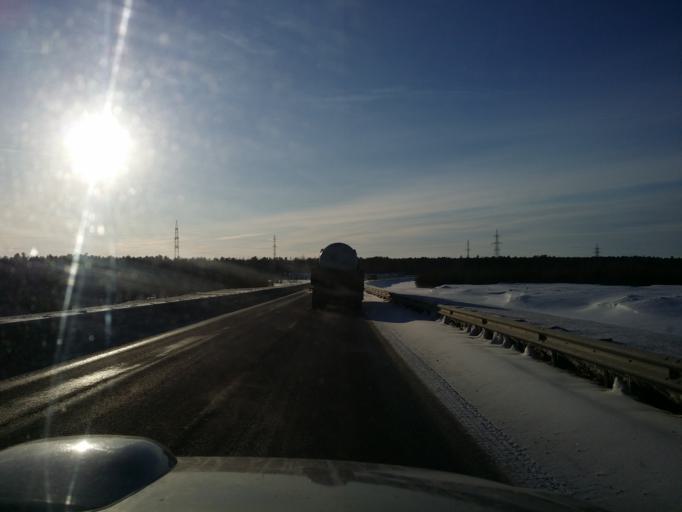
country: RU
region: Khanty-Mansiyskiy Avtonomnyy Okrug
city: Izluchinsk
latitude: 60.9353
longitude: 76.8786
